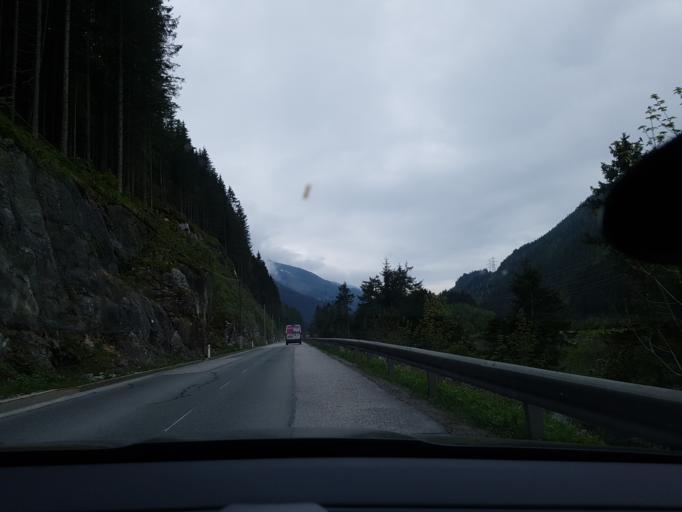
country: AT
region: Tyrol
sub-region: Politischer Bezirk Schwaz
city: Gerlos
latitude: 47.2093
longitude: 11.9990
